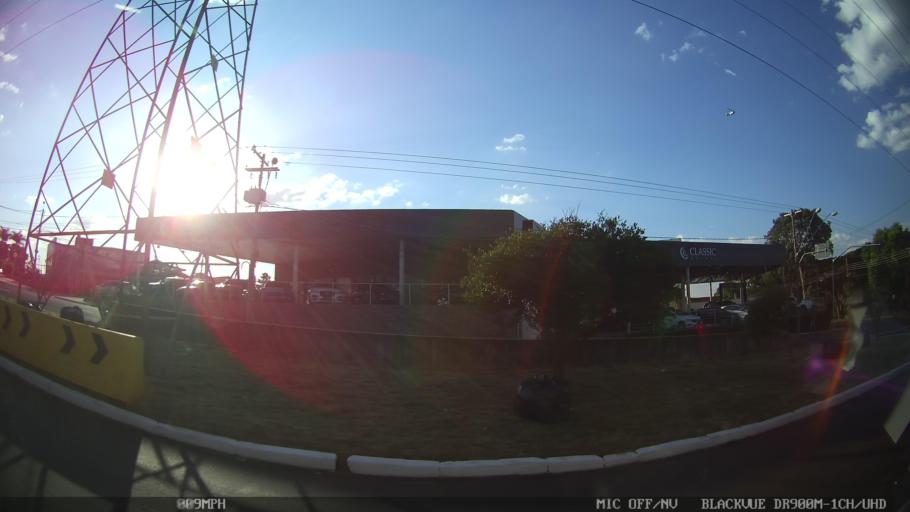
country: BR
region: Sao Paulo
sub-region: Ribeirao Preto
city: Ribeirao Preto
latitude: -21.1959
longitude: -47.8065
